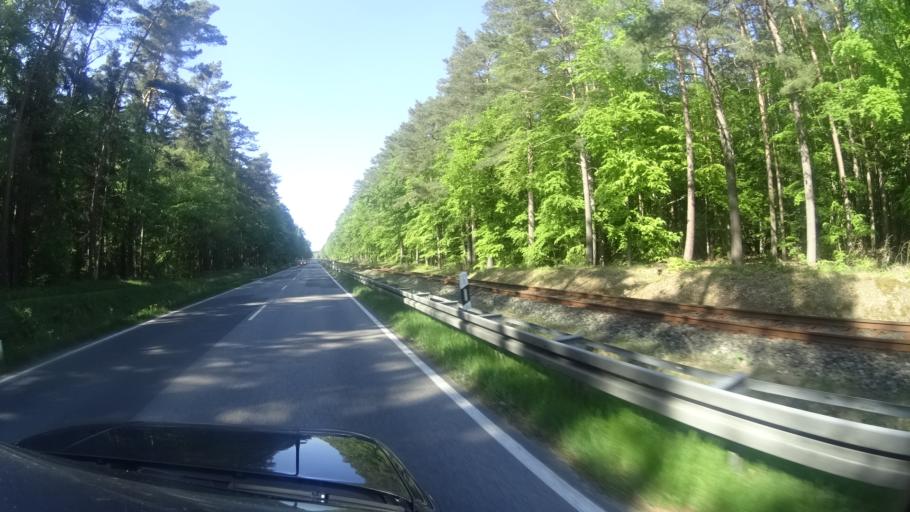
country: DE
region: Mecklenburg-Vorpommern
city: Seeheilbad Graal-Muritz
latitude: 54.2282
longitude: 12.2246
